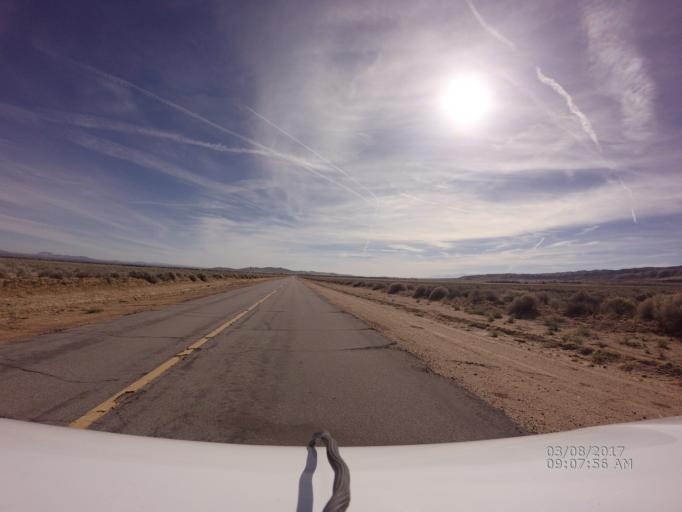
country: US
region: California
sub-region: Los Angeles County
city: Green Valley
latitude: 34.7461
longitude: -118.4832
